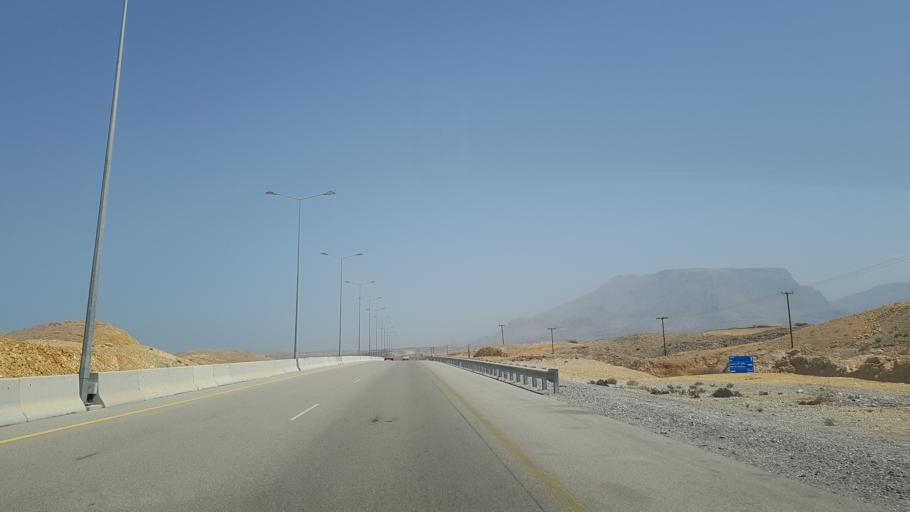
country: OM
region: Ash Sharqiyah
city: Al Qabil
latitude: 23.1093
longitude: 58.9816
